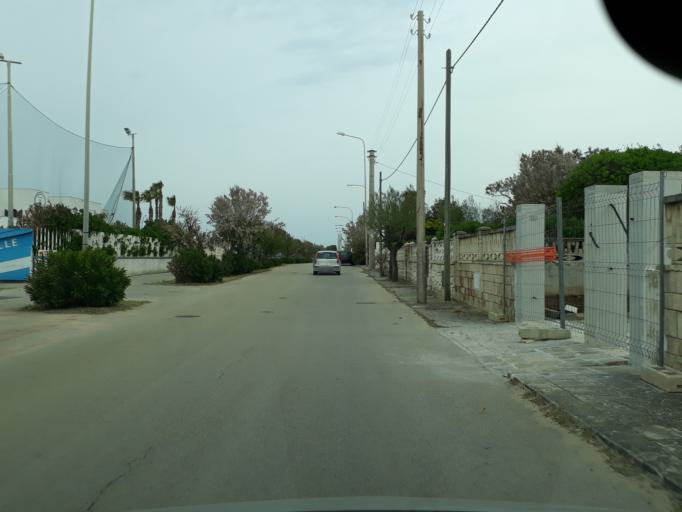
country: IT
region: Apulia
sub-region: Provincia di Brindisi
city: Ostuni
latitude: 40.7862
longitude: 17.5984
